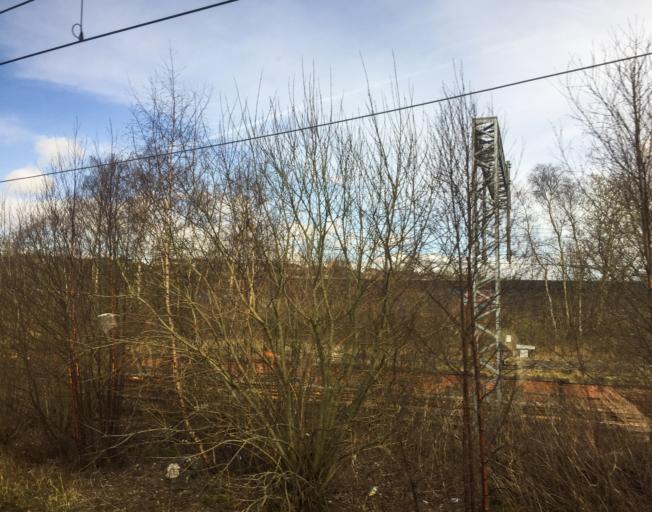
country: GB
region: Scotland
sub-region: East Dunbartonshire
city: Bishopbriggs
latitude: 55.8784
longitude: -4.2245
